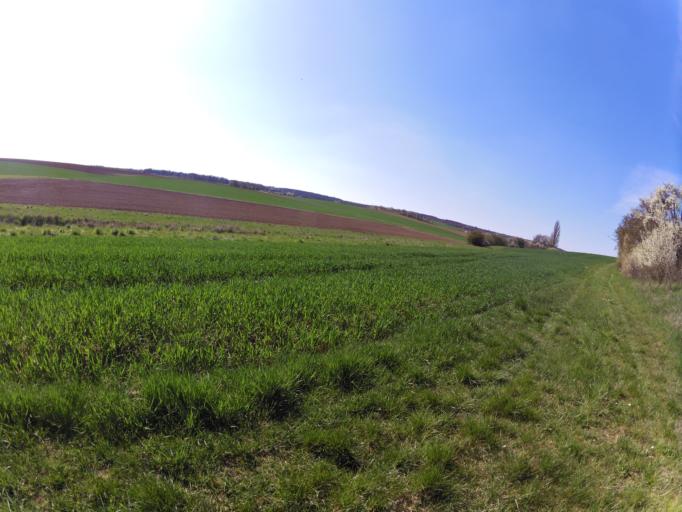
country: DE
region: Bavaria
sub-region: Regierungsbezirk Unterfranken
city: Kurnach
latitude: 49.8700
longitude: 10.0129
